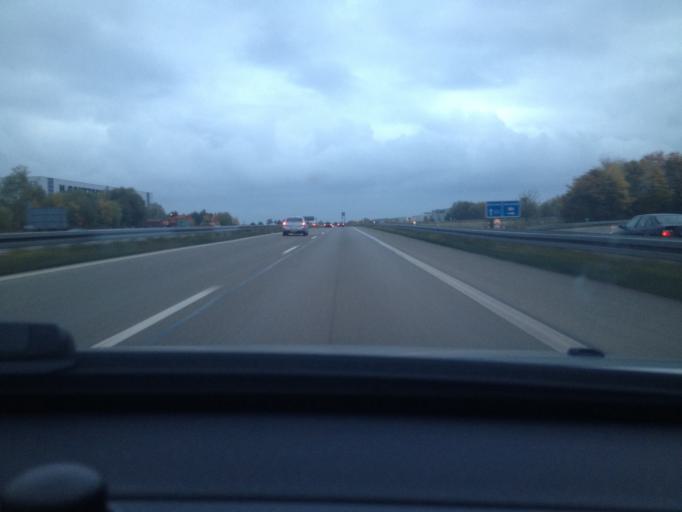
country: DE
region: Baden-Wuerttemberg
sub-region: Tuebingen Region
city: Dornstadt
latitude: 48.4563
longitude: 9.9635
